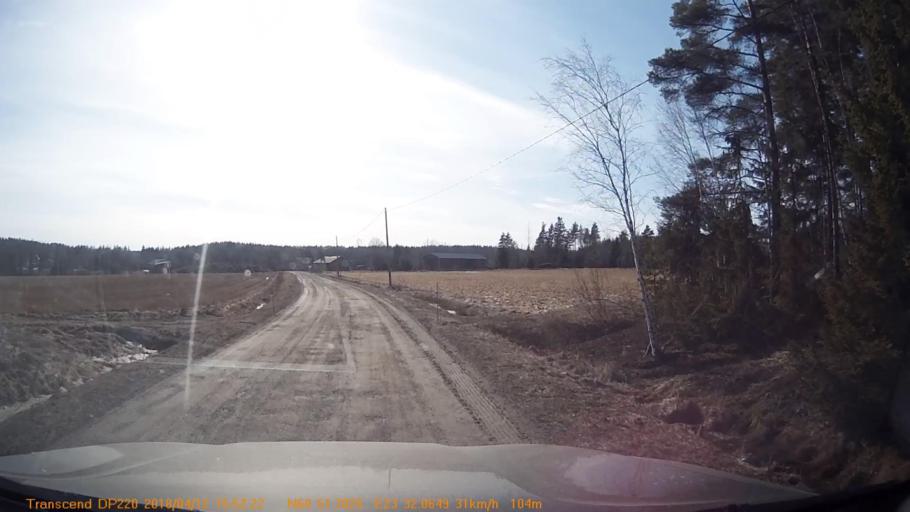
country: FI
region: Haeme
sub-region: Forssa
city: Jokioinen
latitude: 60.8630
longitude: 23.5340
